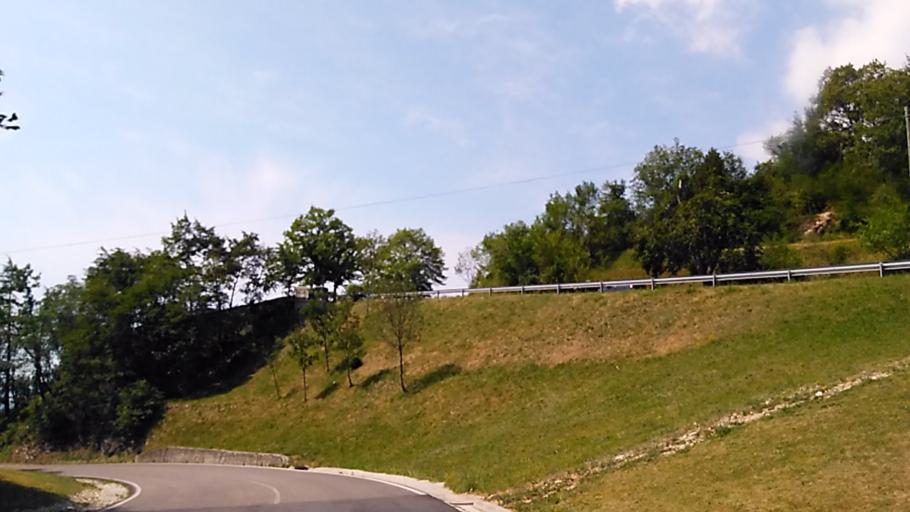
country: IT
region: Lombardy
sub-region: Provincia di Brescia
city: Gardola
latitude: 45.7395
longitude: 10.7296
